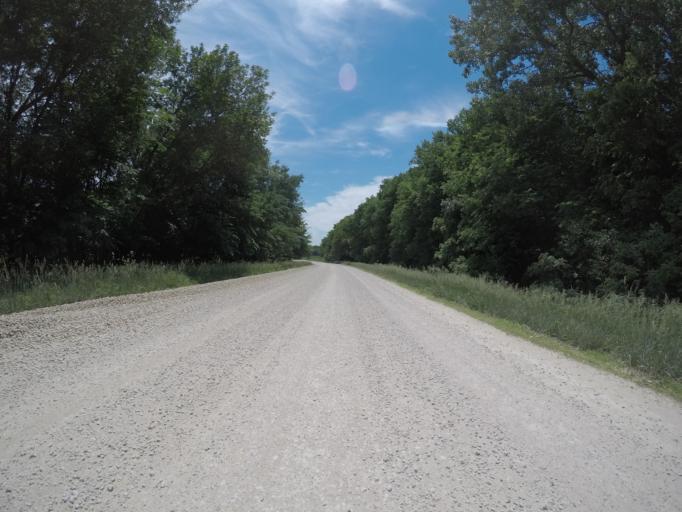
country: US
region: Kansas
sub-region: Wabaunsee County
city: Alma
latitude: 38.9582
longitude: -96.2520
